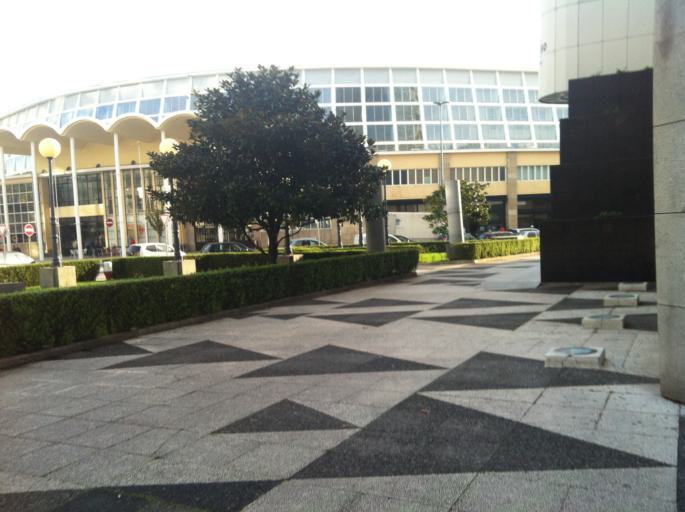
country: PT
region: Porto
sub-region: Porto
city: Porto
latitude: 41.1554
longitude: -8.6300
